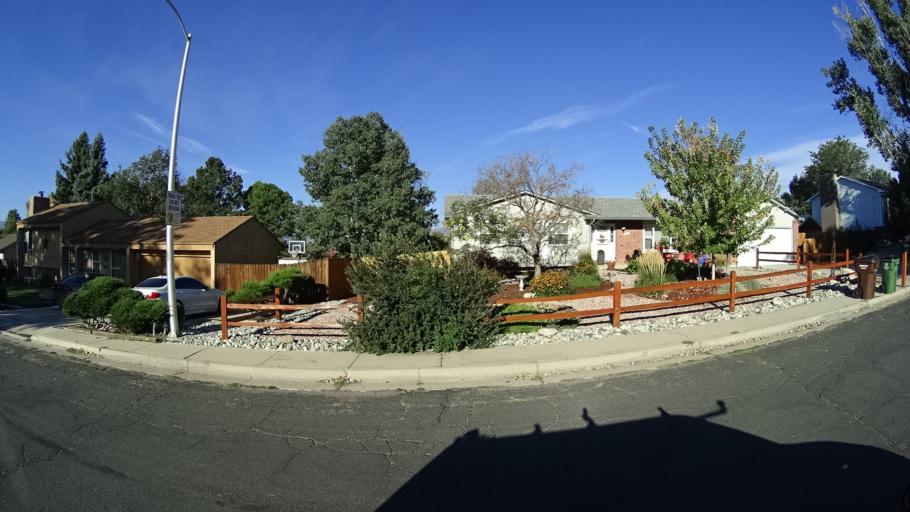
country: US
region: Colorado
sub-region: El Paso County
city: Cimarron Hills
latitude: 38.9050
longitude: -104.7527
